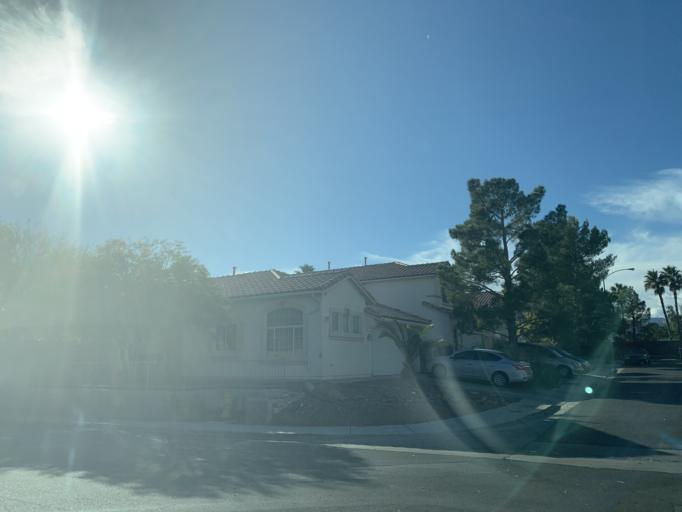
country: US
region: Nevada
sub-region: Clark County
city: Summerlin South
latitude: 36.1280
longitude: -115.3086
